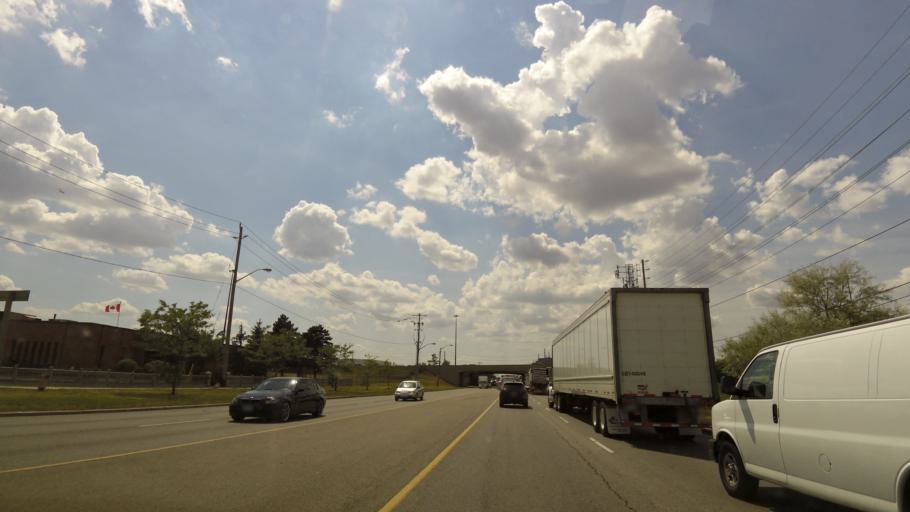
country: CA
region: Ontario
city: Concord
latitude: 43.7732
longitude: -79.5325
